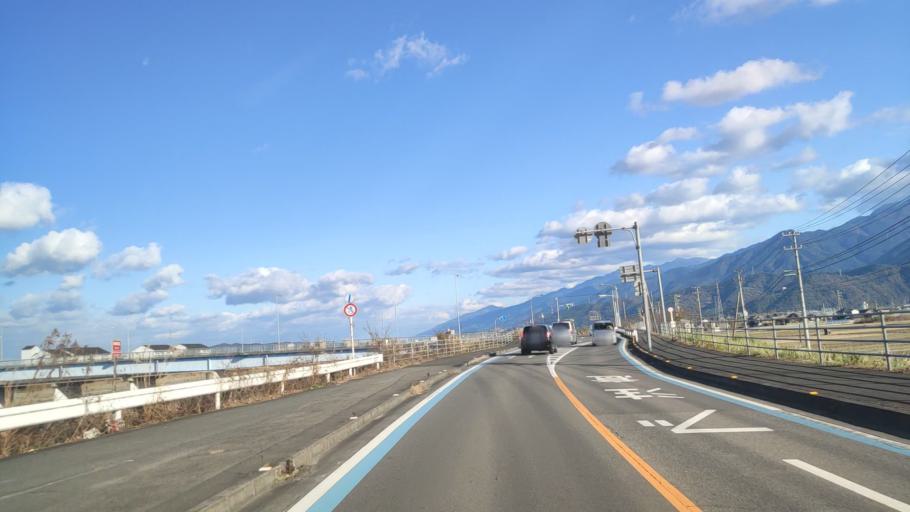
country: JP
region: Ehime
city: Saijo
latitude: 33.9113
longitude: 133.1599
